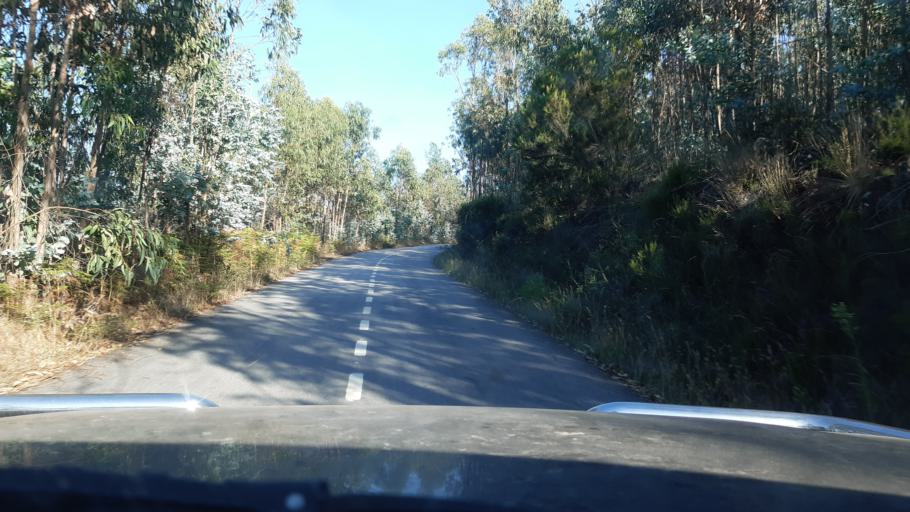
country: PT
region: Aveiro
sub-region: Agueda
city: Aguada de Cima
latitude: 40.5653
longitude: -8.3156
